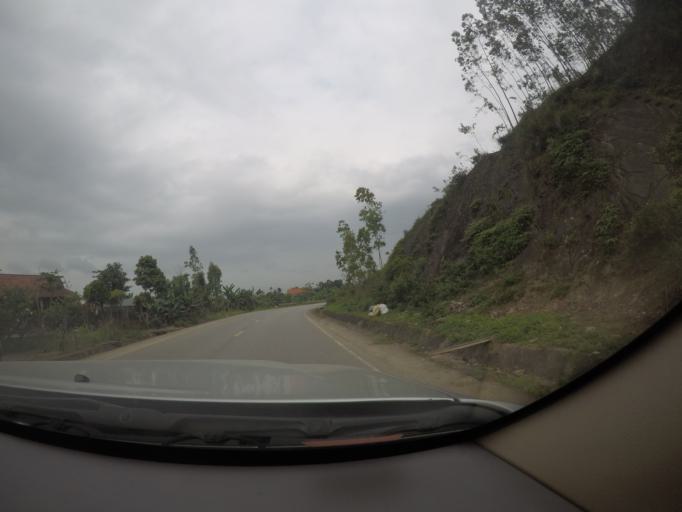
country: VN
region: Quang Binh
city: Ba Don
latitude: 17.6166
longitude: 106.3565
